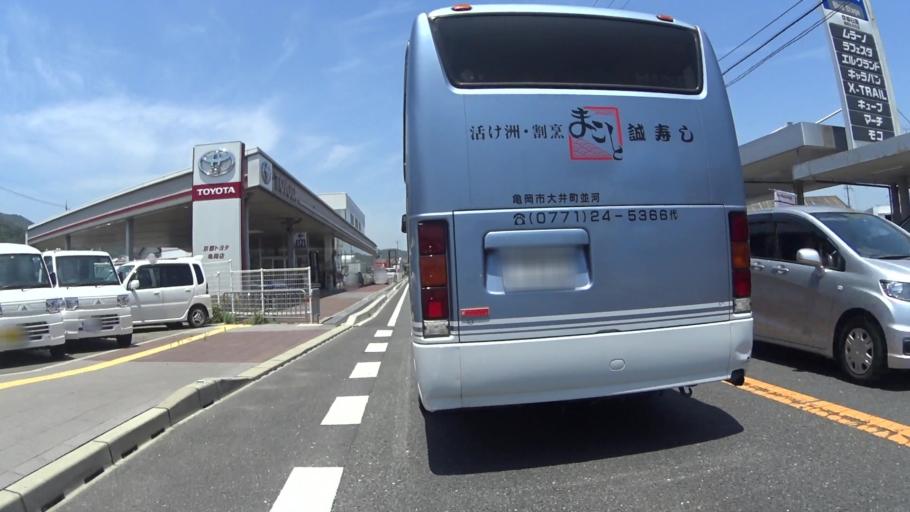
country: JP
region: Kyoto
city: Kameoka
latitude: 35.0369
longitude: 135.5486
